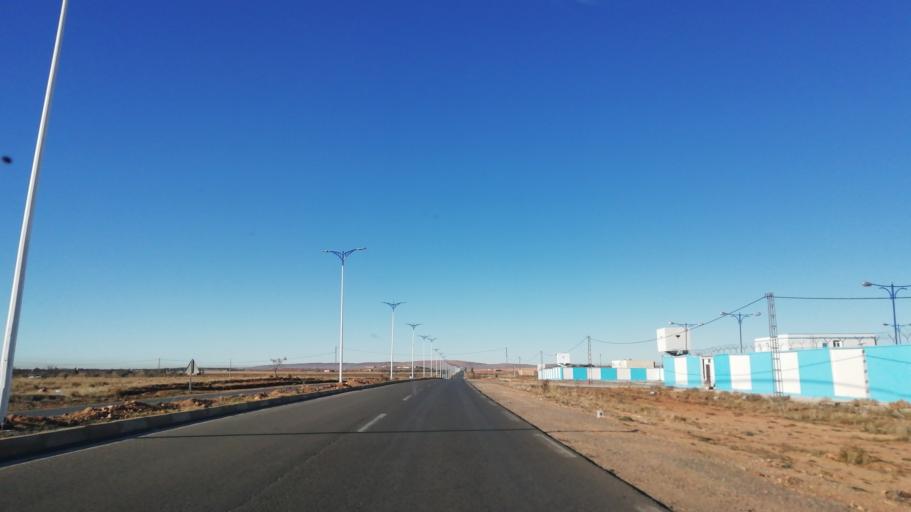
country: DZ
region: El Bayadh
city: El Bayadh
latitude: 33.6913
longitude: 1.0745
